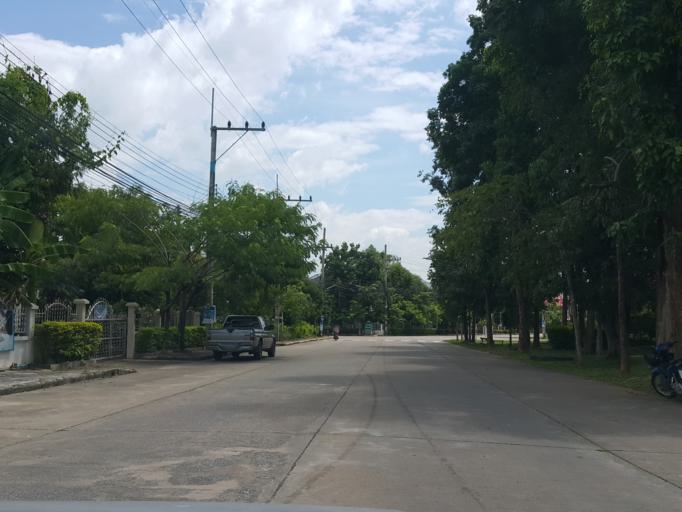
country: TH
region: Chiang Mai
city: Hang Dong
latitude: 18.7414
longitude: 98.9416
